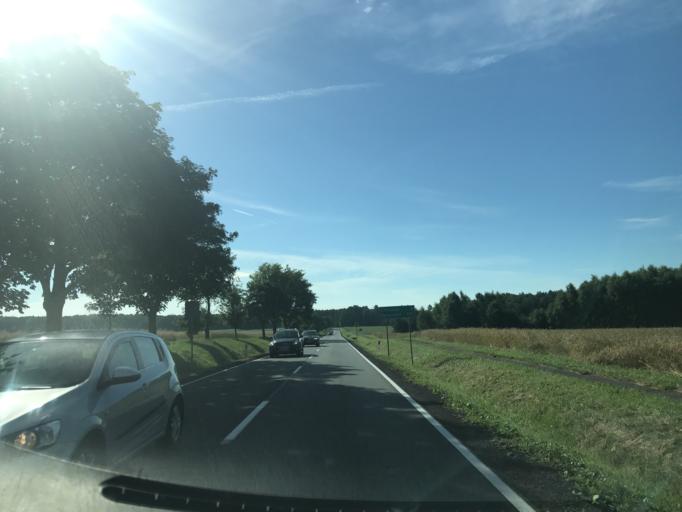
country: PL
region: Pomeranian Voivodeship
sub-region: Powiat czluchowski
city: Przechlewo
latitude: 53.7081
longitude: 17.2612
